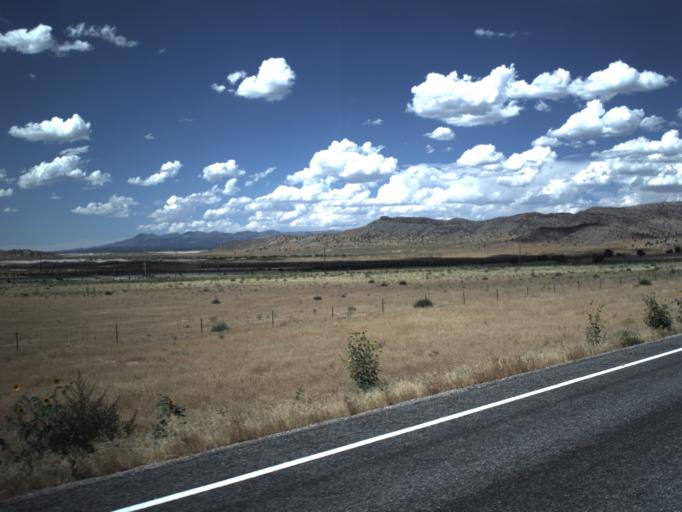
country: US
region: Utah
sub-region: Millard County
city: Delta
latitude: 39.6416
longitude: -112.3038
